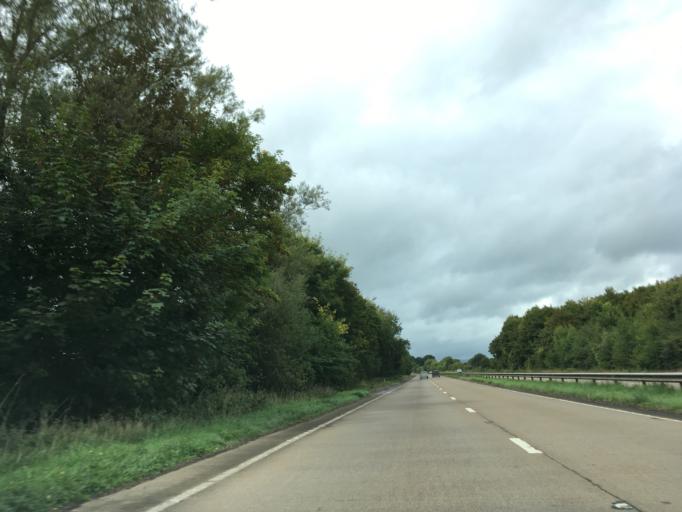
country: GB
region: Wales
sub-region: Monmouthshire
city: Llanarth
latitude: 51.7692
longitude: -2.8673
